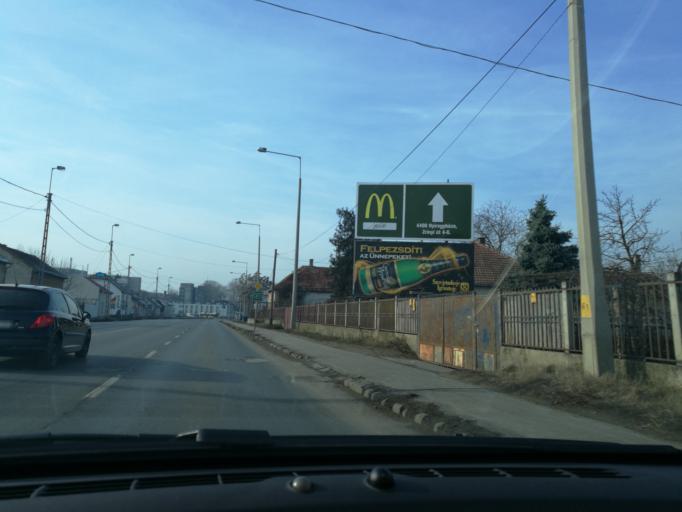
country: HU
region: Szabolcs-Szatmar-Bereg
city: Nyiregyhaza
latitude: 47.9521
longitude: 21.7378
